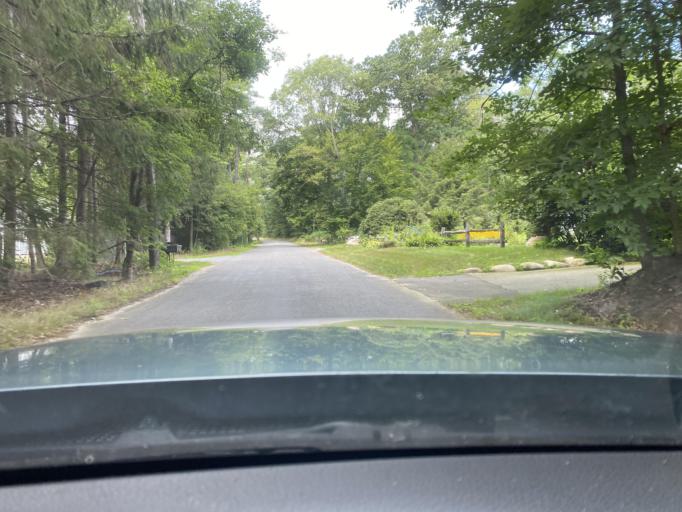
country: US
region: Massachusetts
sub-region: Norfolk County
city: Medfield
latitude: 42.1804
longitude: -71.3324
